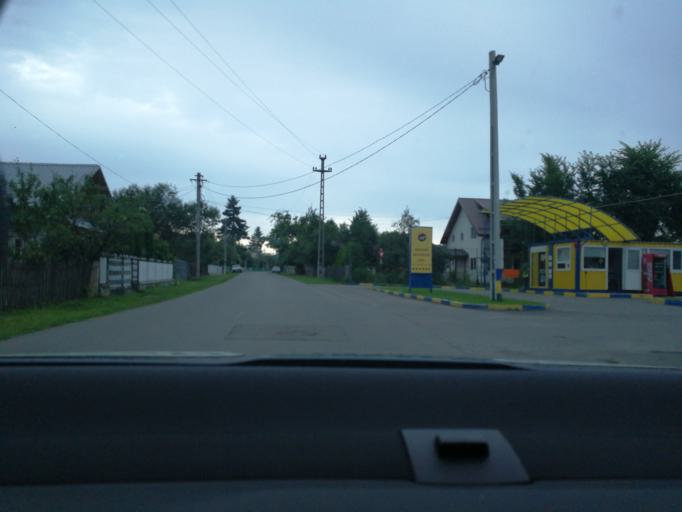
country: RO
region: Prahova
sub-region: Comuna Brebu
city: Brebu Megiesesc
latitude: 45.1670
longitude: 25.7709
